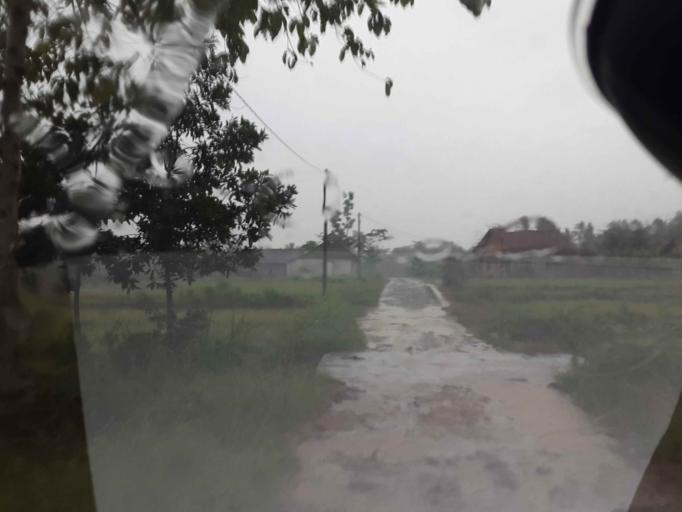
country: ID
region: Lampung
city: Kedaton
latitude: -5.3922
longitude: 105.3342
